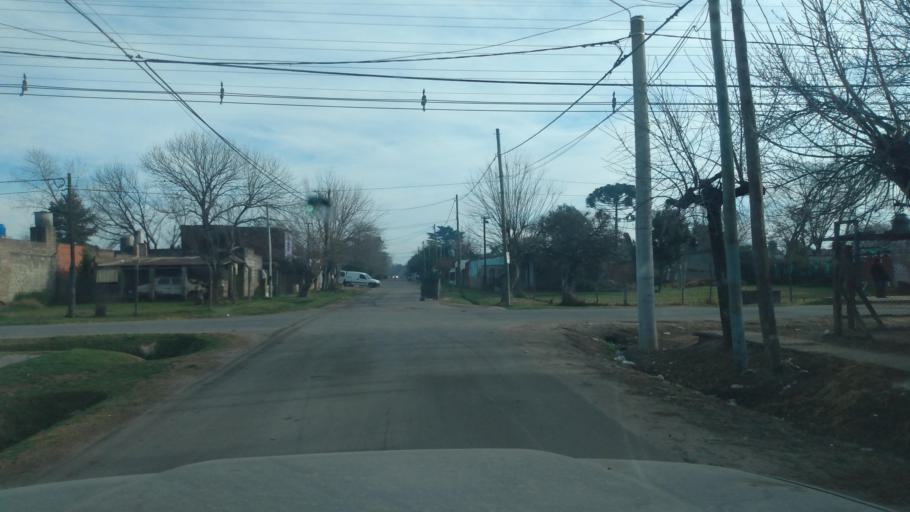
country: AR
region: Buenos Aires
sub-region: Partido de Lujan
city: Lujan
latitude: -34.5455
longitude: -59.1183
